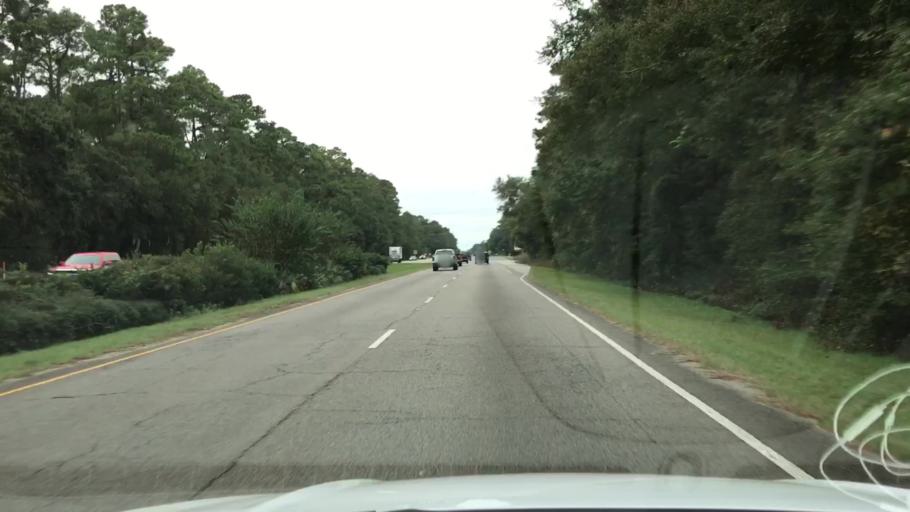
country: US
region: South Carolina
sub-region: Georgetown County
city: Murrells Inlet
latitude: 33.5203
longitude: -79.0685
